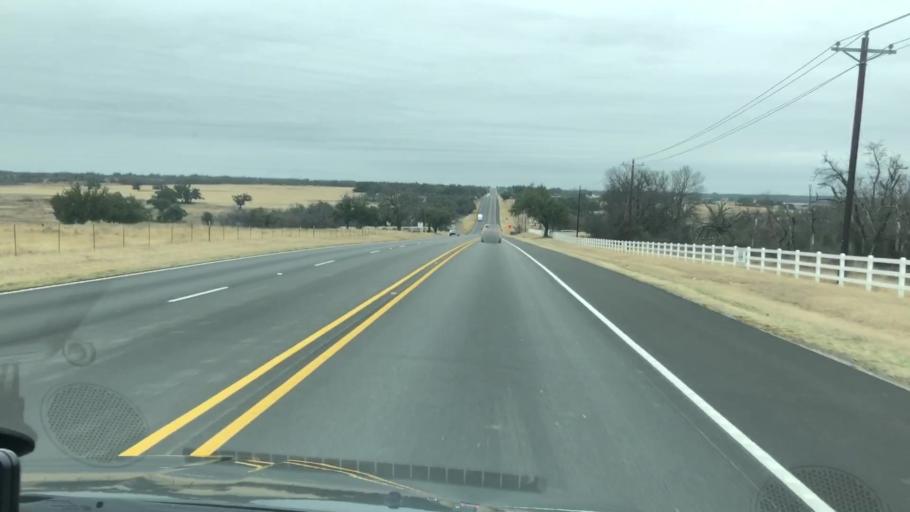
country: US
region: Texas
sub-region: Erath County
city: Stephenville
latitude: 32.2988
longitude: -98.1882
